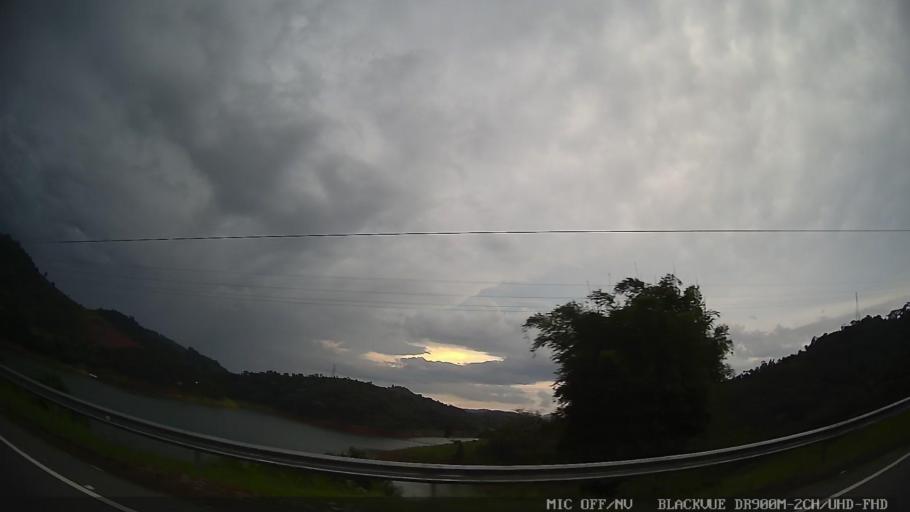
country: BR
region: Sao Paulo
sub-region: Caraguatatuba
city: Caraguatatuba
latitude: -23.4792
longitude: -45.5810
